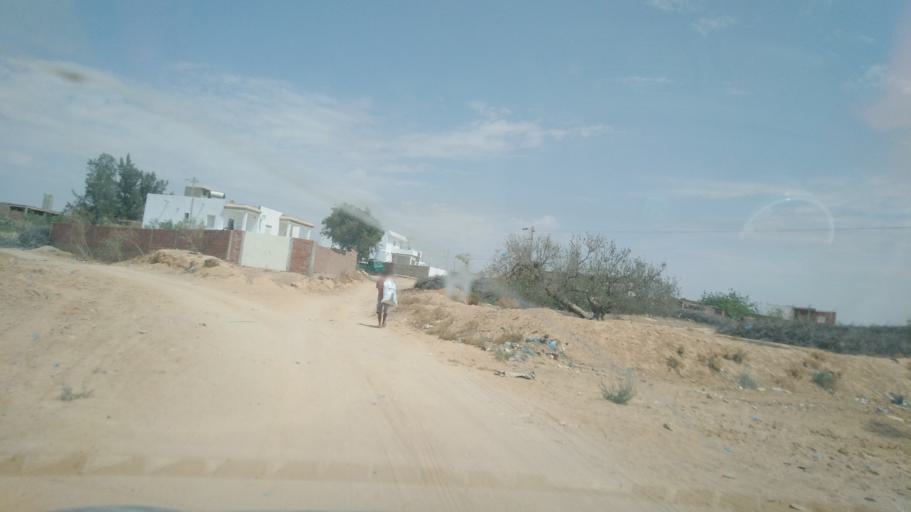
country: TN
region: Safaqis
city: Sfax
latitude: 34.7400
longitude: 10.5608
